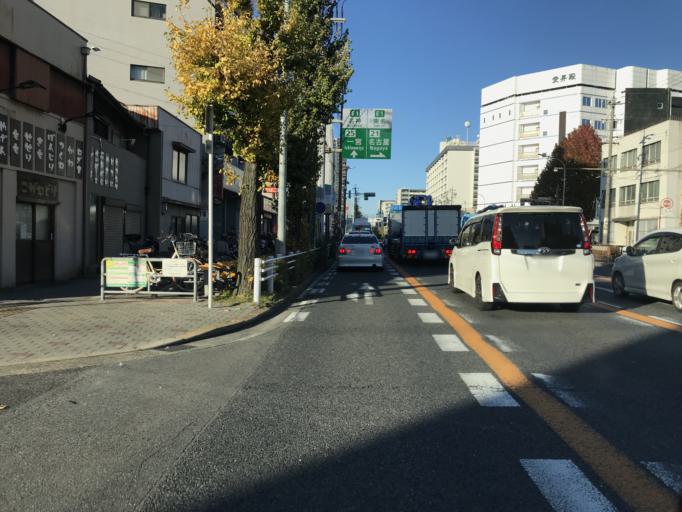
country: JP
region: Aichi
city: Nagoya-shi
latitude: 35.1669
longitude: 136.8721
